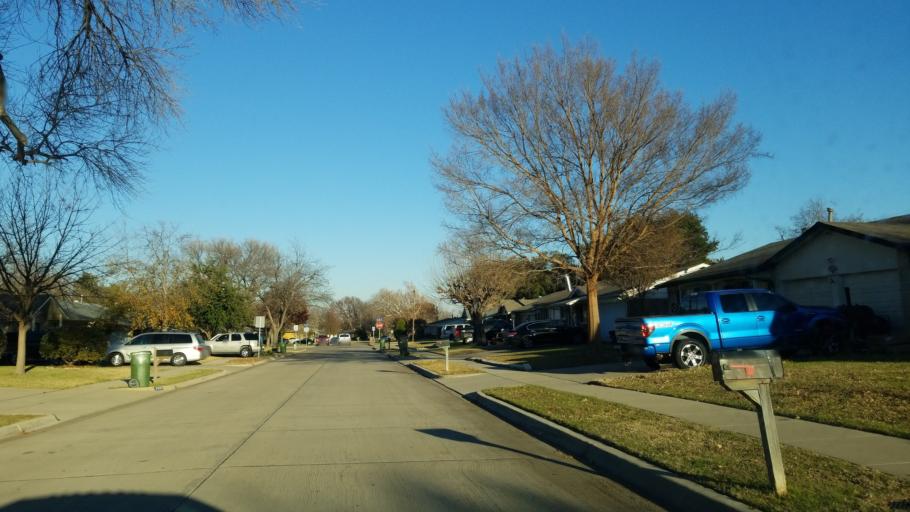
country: US
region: Texas
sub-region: Tarrant County
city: Arlington
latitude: 32.7237
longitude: -97.0677
